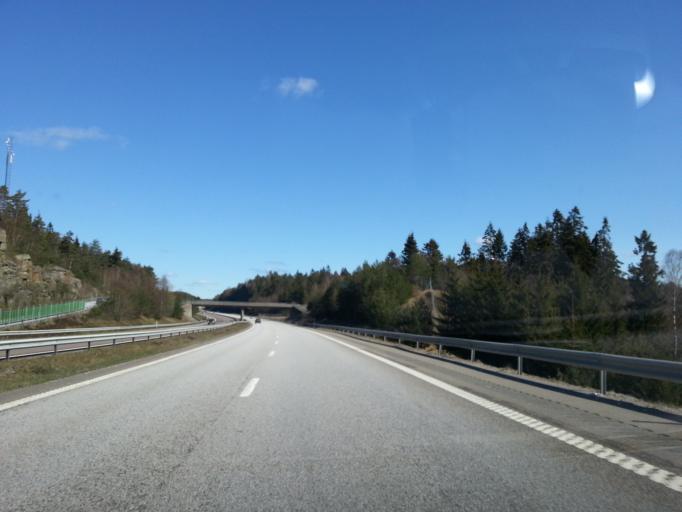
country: SE
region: Vaestra Goetaland
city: Svanesund
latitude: 58.1517
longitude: 11.8863
